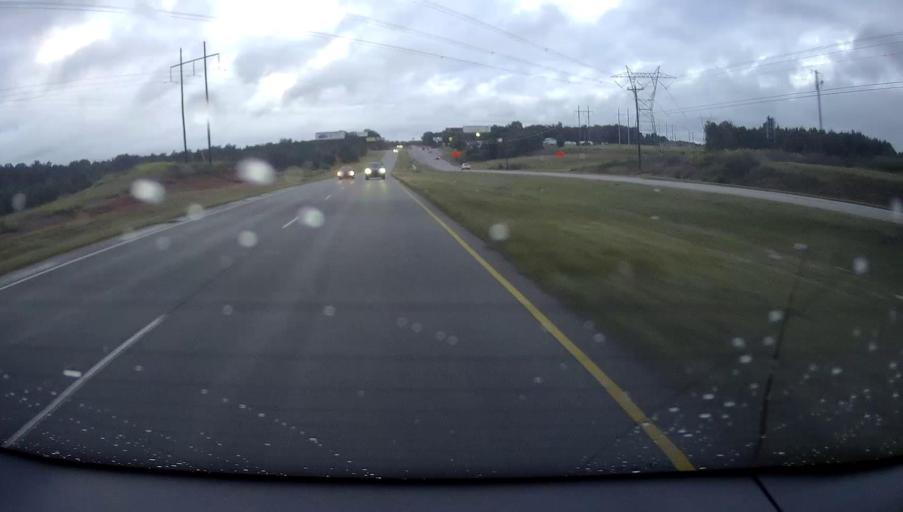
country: US
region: Georgia
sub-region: Houston County
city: Centerville
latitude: 32.6142
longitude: -83.7194
